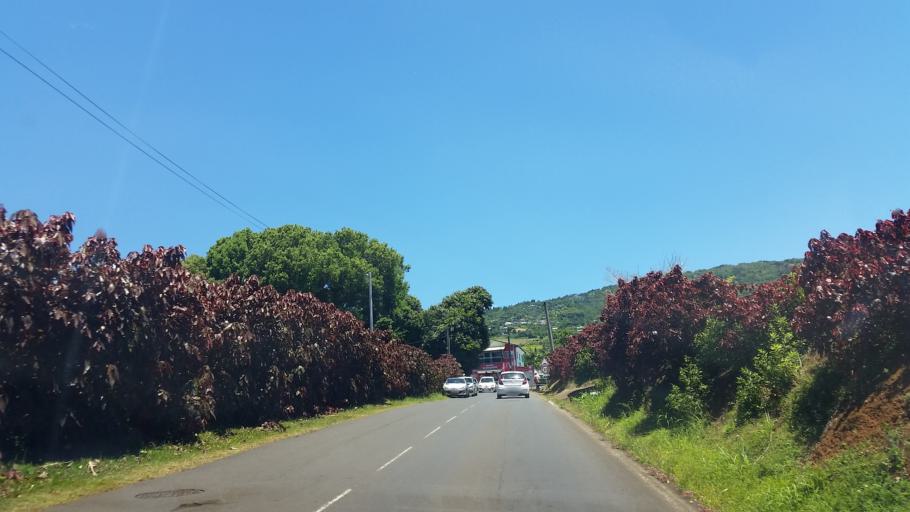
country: RE
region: Reunion
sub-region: Reunion
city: Sainte-Marie
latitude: -20.9293
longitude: 55.5307
